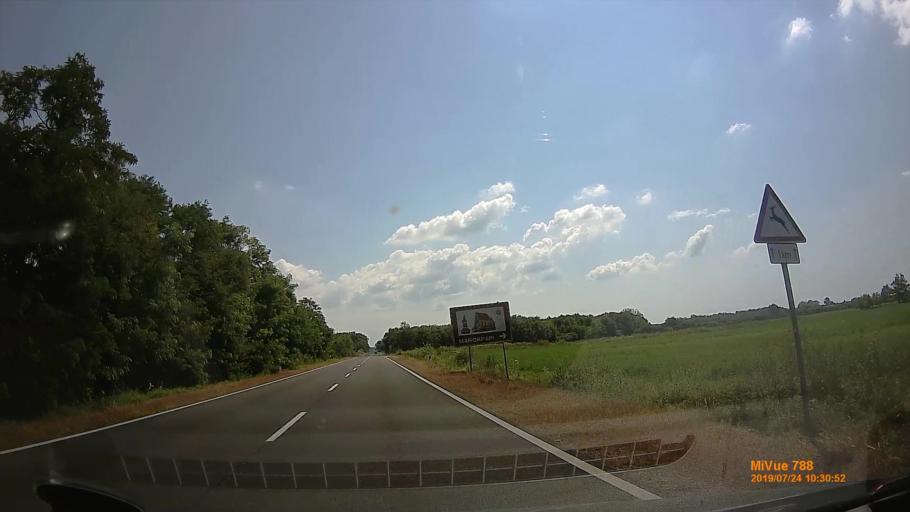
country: HU
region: Szabolcs-Szatmar-Bereg
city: Tarpa
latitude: 48.1606
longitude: 22.4991
